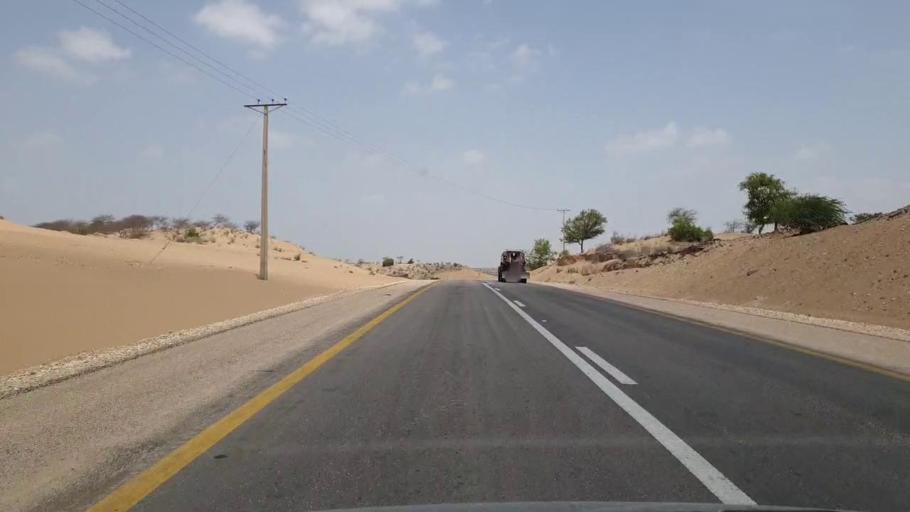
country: PK
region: Sindh
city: Mithi
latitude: 24.8004
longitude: 69.7370
